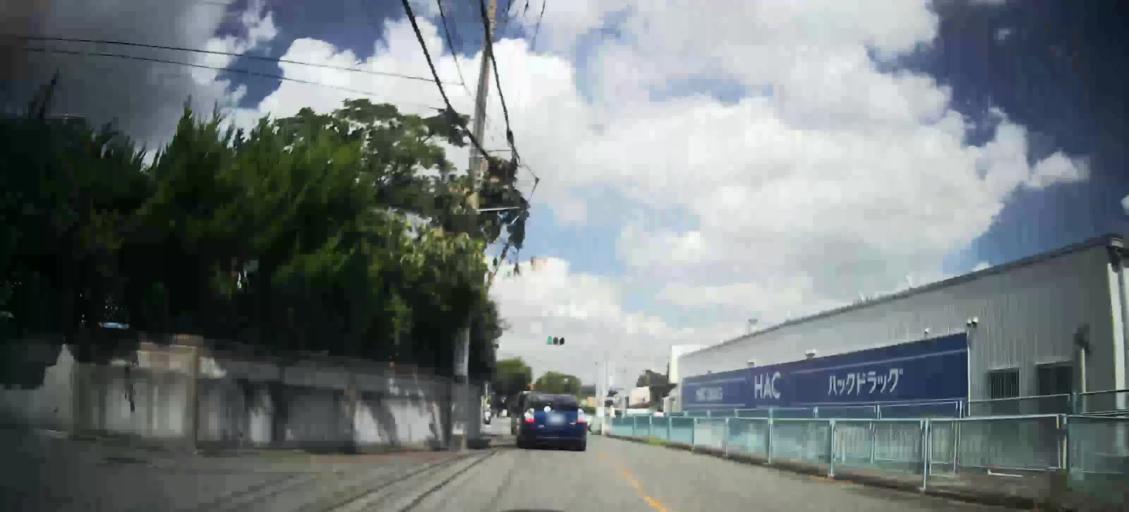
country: JP
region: Kanagawa
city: Yokohama
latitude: 35.4580
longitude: 139.5617
